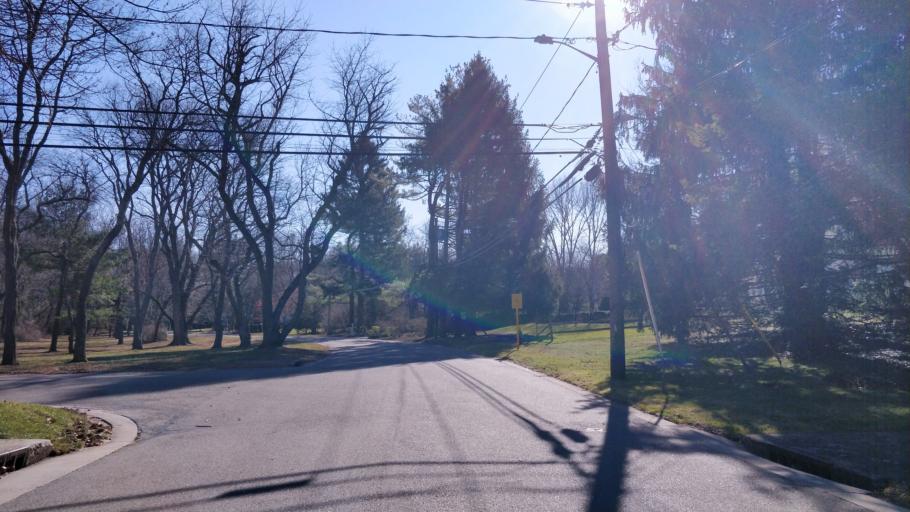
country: US
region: New York
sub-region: Nassau County
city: Upper Brookville
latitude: 40.8500
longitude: -73.5610
